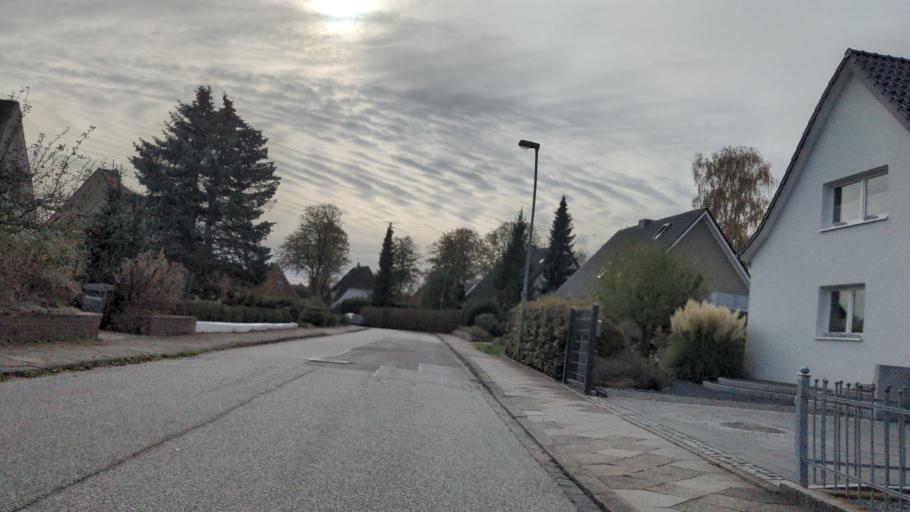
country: DE
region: Mecklenburg-Vorpommern
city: Selmsdorf
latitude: 53.9135
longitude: 10.8215
